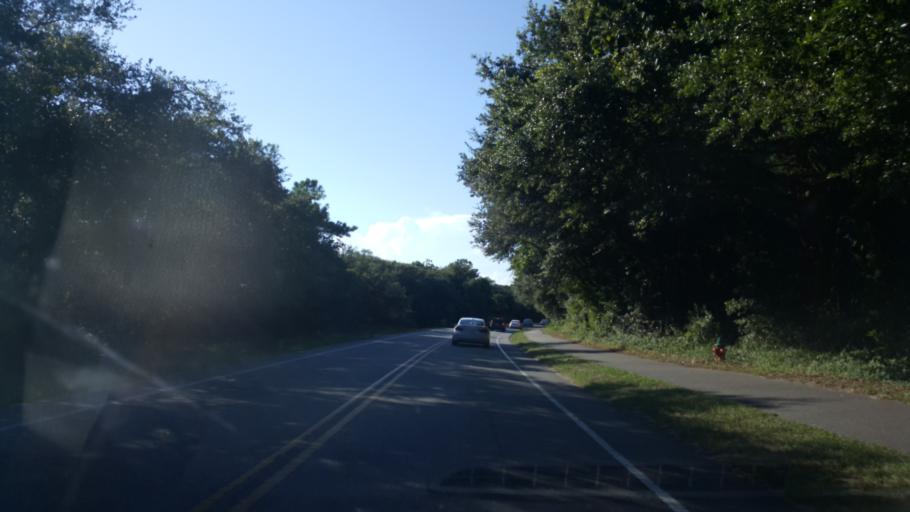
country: US
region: North Carolina
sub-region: Dare County
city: Southern Shores
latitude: 36.1325
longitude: -75.7336
